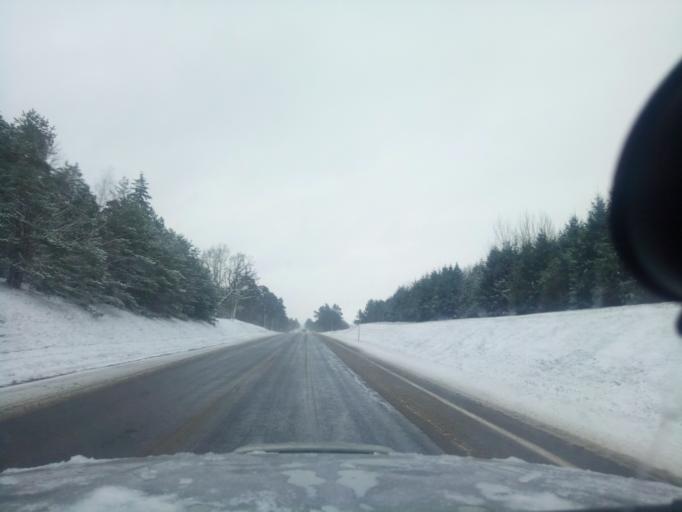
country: BY
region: Minsk
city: Nyasvizh
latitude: 53.2607
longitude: 26.6106
